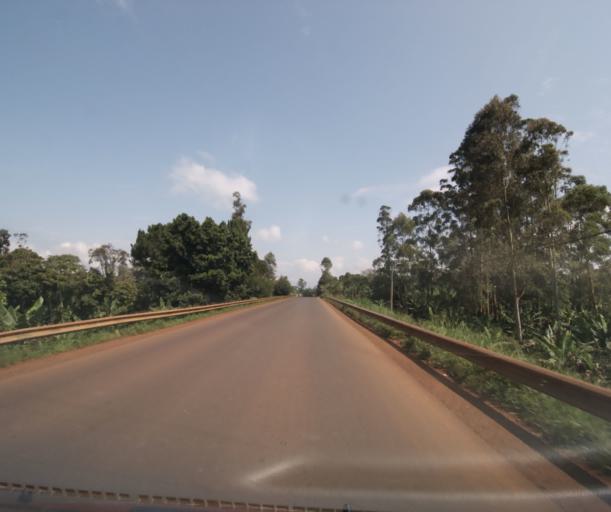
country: CM
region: West
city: Bansoa
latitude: 5.4865
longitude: 10.2684
